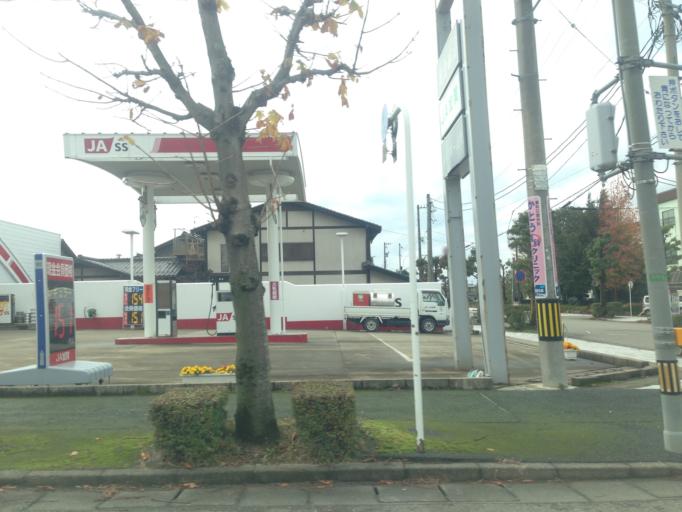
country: JP
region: Ishikawa
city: Komatsu
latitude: 36.2965
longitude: 136.3594
